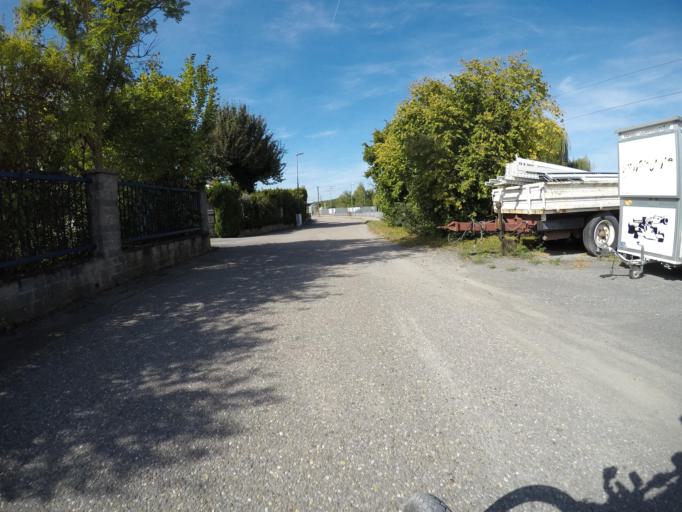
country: DE
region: Baden-Wuerttemberg
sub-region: Karlsruhe Region
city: Bretten
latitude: 49.1209
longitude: 8.7272
